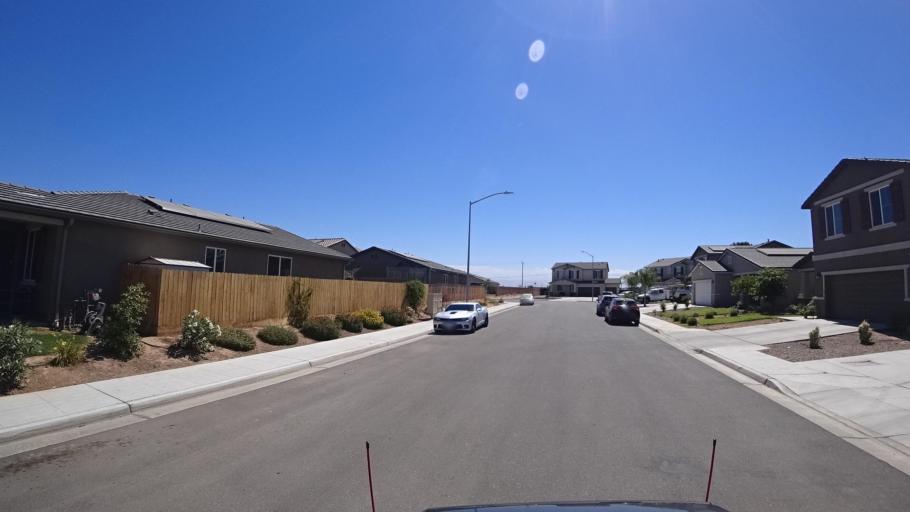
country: US
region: California
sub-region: Fresno County
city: Sunnyside
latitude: 36.7189
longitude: -119.6656
